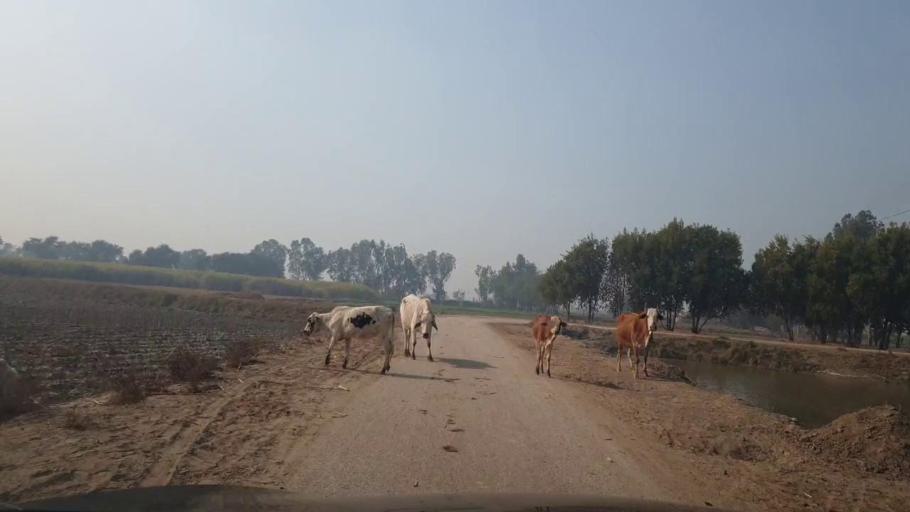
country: PK
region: Sindh
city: Ubauro
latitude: 28.1212
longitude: 69.8216
